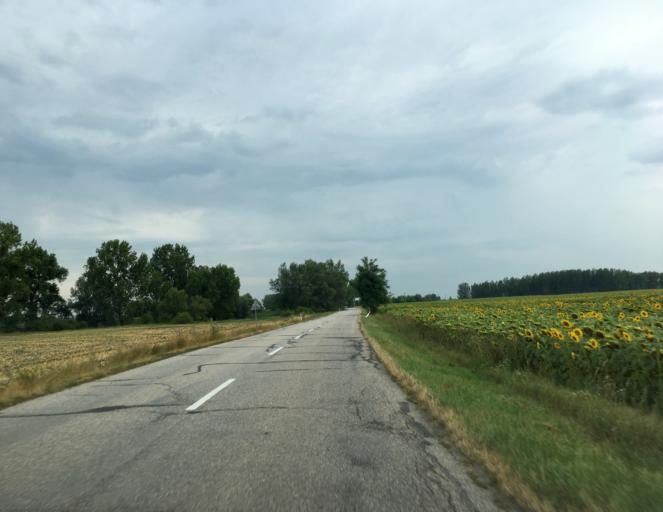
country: SK
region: Nitriansky
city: Kolarovo
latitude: 47.8962
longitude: 17.9240
